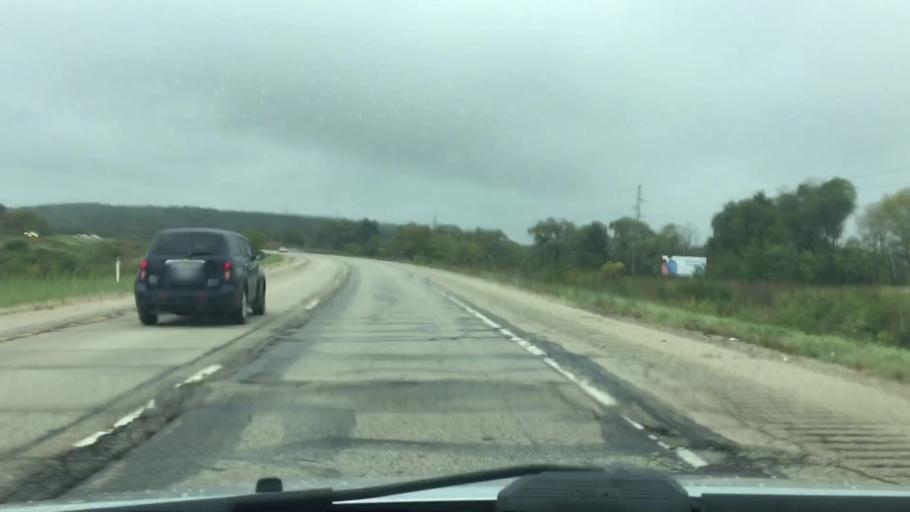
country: US
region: Wisconsin
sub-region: Walworth County
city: Como
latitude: 42.6177
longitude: -88.4586
